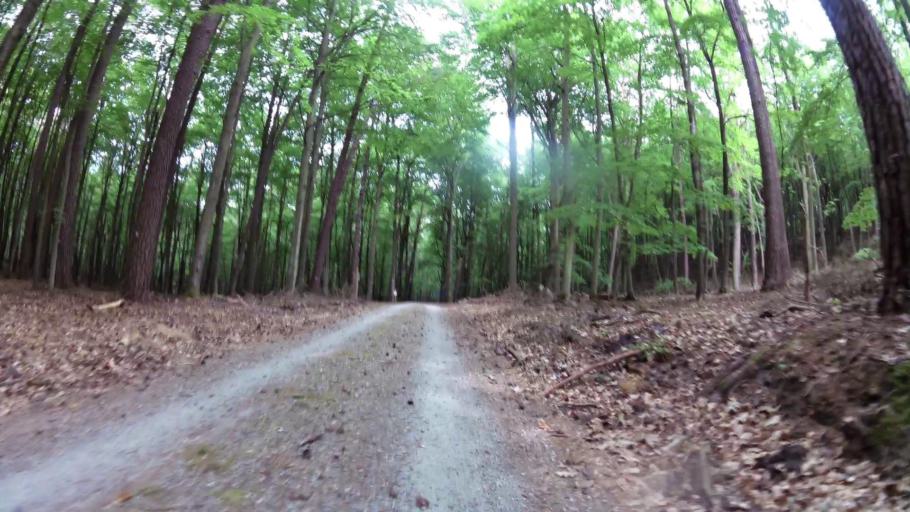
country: PL
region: West Pomeranian Voivodeship
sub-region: Powiat kamienski
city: Miedzyzdroje
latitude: 53.9470
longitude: 14.5178
